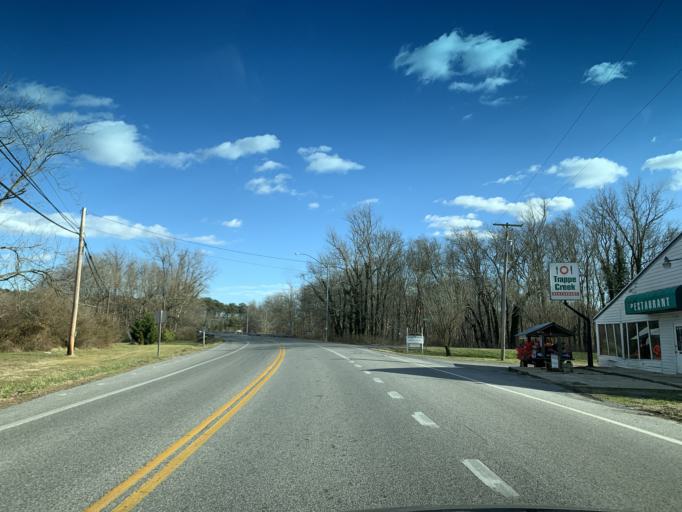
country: US
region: Maryland
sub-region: Worcester County
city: Berlin
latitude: 38.3146
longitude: -75.1937
